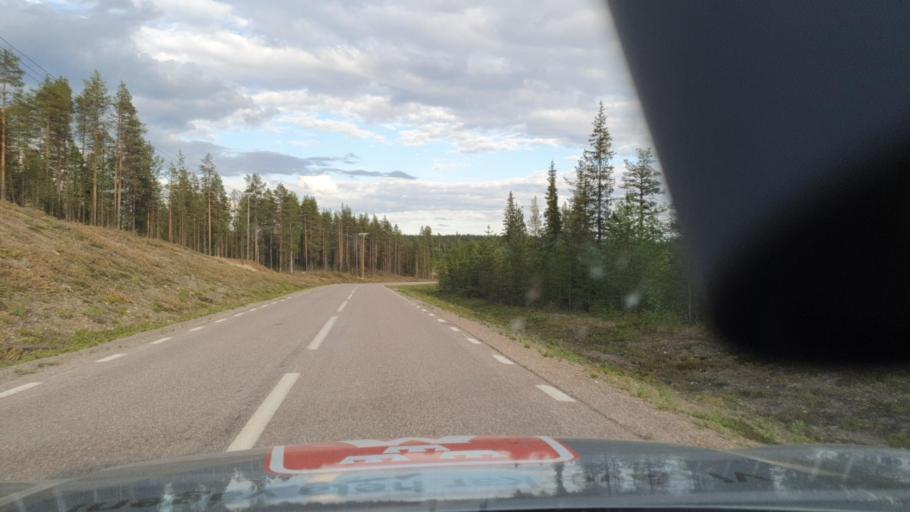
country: SE
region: Norrbotten
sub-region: Gallivare Kommun
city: Gaellivare
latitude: 66.9449
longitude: 21.2428
